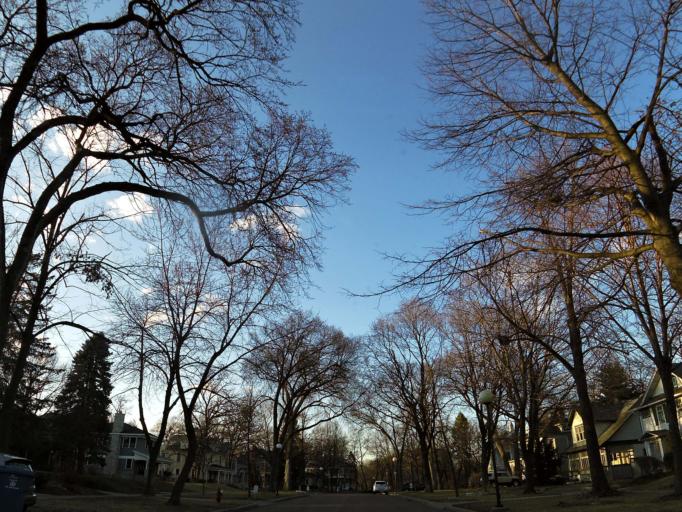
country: US
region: Minnesota
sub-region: Hennepin County
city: Saint Louis Park
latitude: 44.9286
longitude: -93.3114
